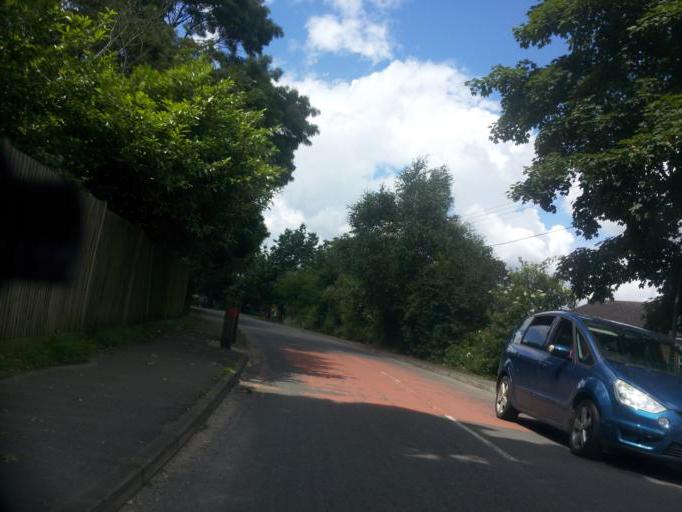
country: GB
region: England
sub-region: Kent
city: West Malling
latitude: 51.3144
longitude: 0.3973
